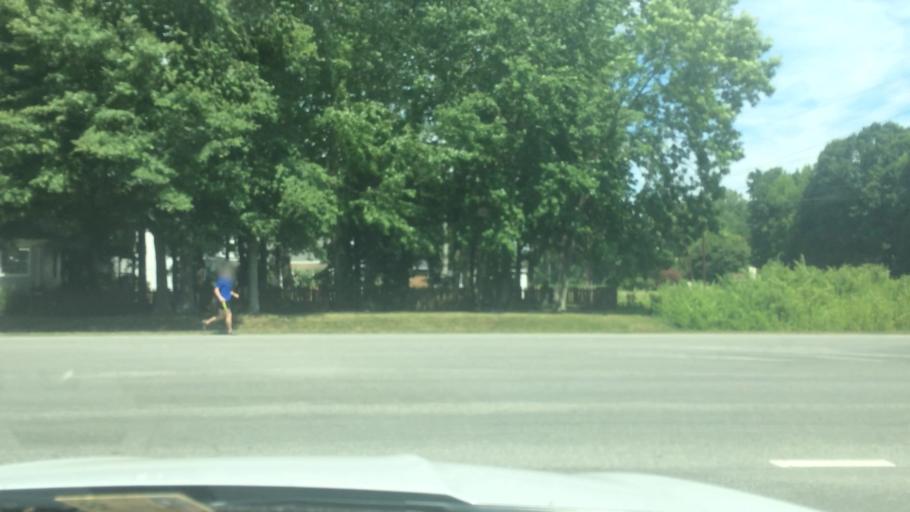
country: US
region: Virginia
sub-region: City of Poquoson
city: Poquoson
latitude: 37.1127
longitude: -76.4240
